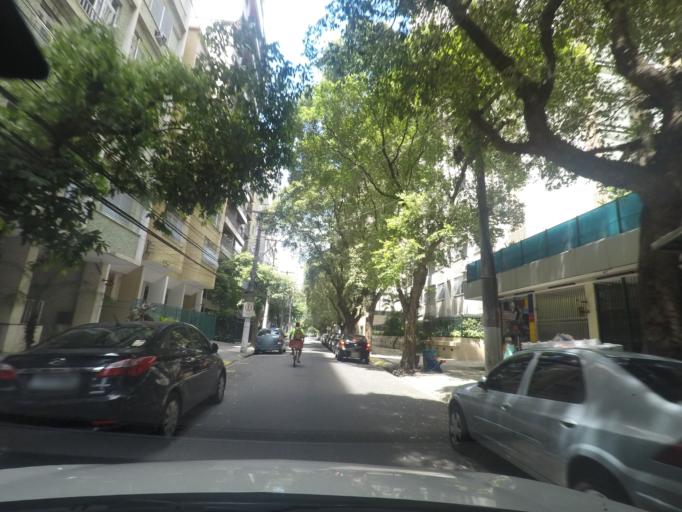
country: BR
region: Rio de Janeiro
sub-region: Niteroi
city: Niteroi
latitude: -22.9060
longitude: -43.1114
